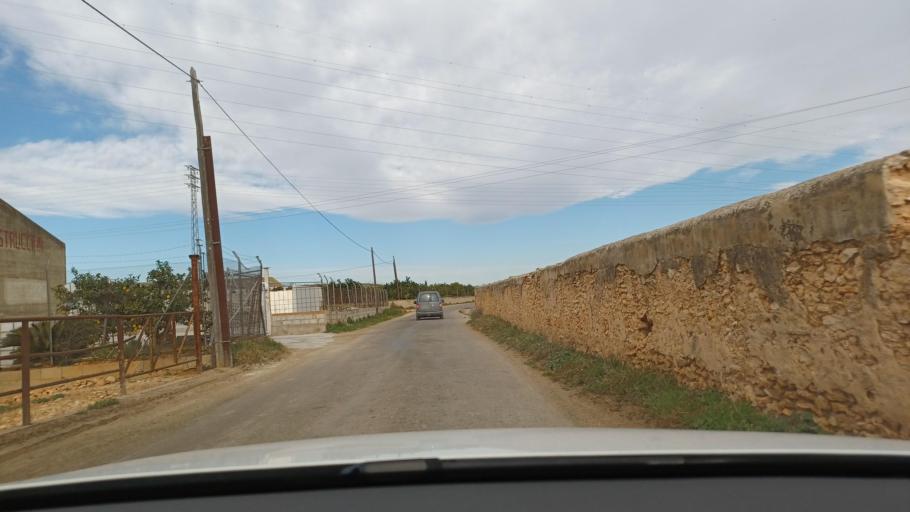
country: ES
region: Valencia
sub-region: Provincia de Valencia
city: Benifaio
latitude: 39.2895
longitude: -0.4344
